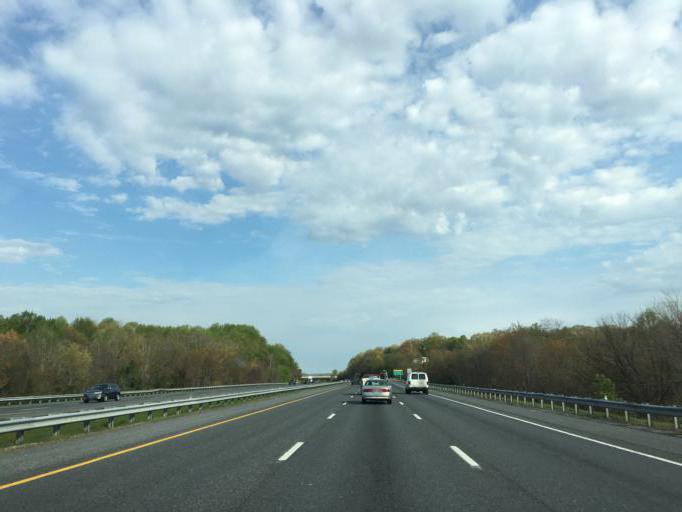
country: US
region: Maryland
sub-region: Frederick County
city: Spring Ridge
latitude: 39.3966
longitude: -77.3296
